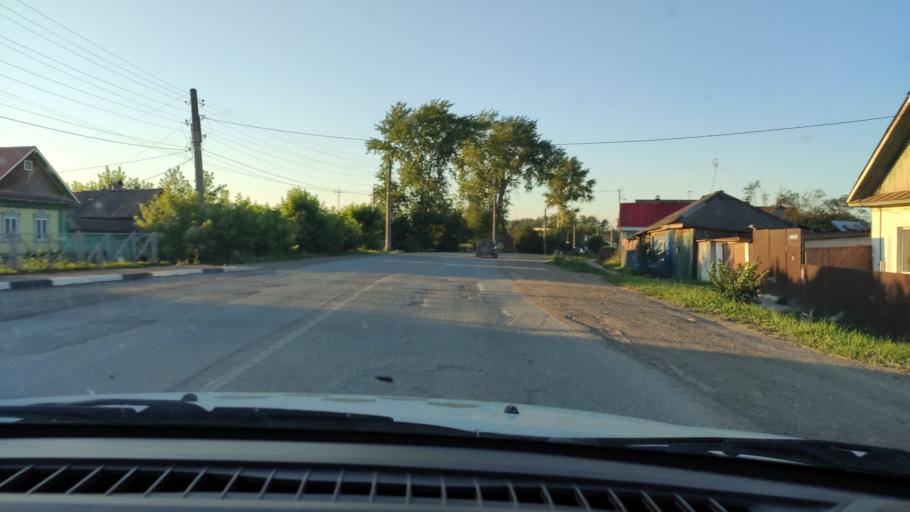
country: RU
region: Perm
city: Kungur
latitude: 57.4263
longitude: 56.9319
